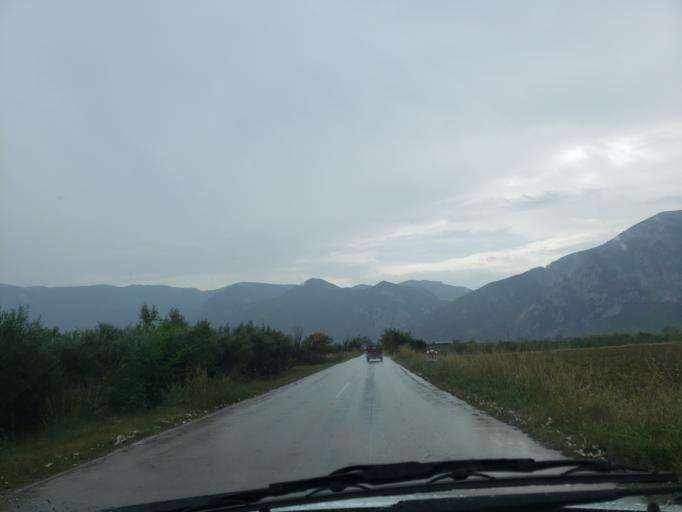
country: GR
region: Central Greece
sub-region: Nomos Fthiotidos
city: Anthili
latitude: 38.8157
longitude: 22.4422
